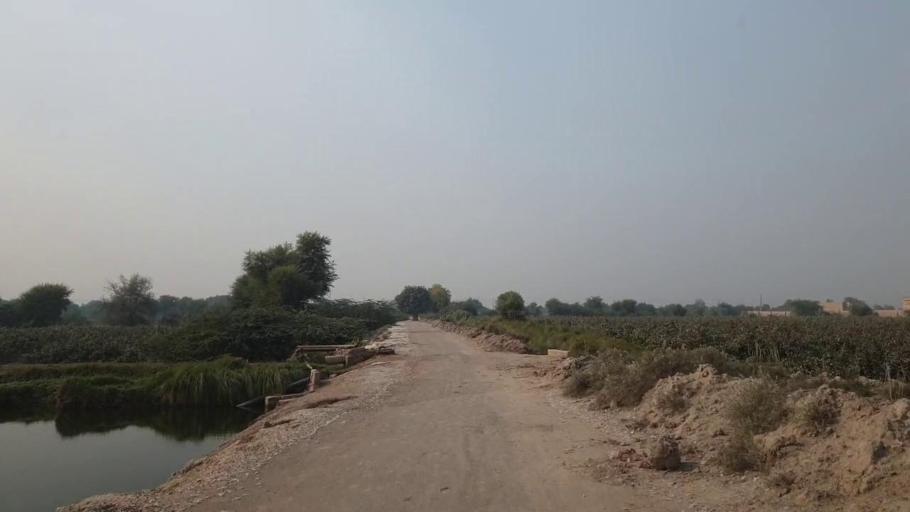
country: PK
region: Sindh
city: Bhan
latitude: 26.5409
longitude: 67.7185
